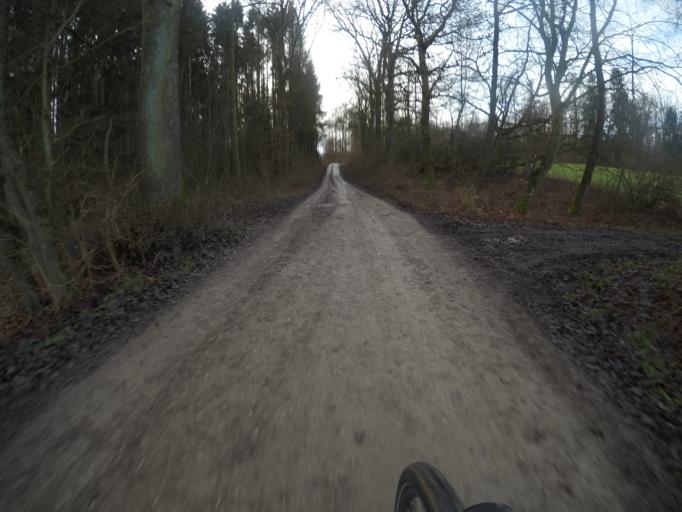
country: DE
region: Baden-Wuerttemberg
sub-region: Regierungsbezirk Stuttgart
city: Unterensingen
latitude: 48.6738
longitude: 9.3400
